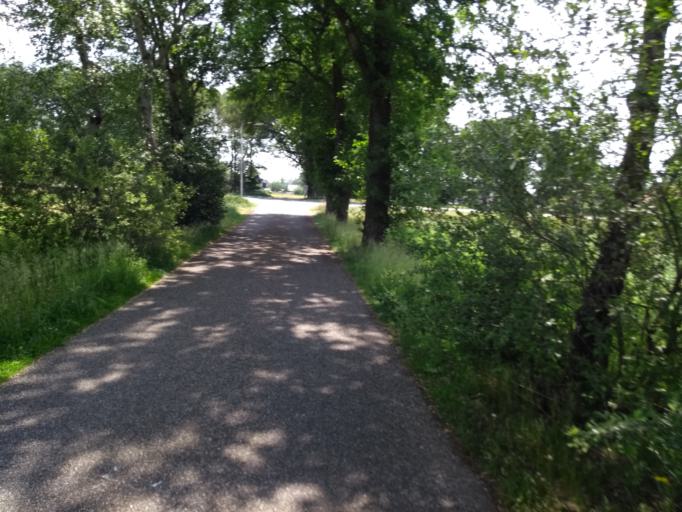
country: NL
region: Overijssel
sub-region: Gemeente Almelo
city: Almelo
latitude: 52.3798
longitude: 6.7188
